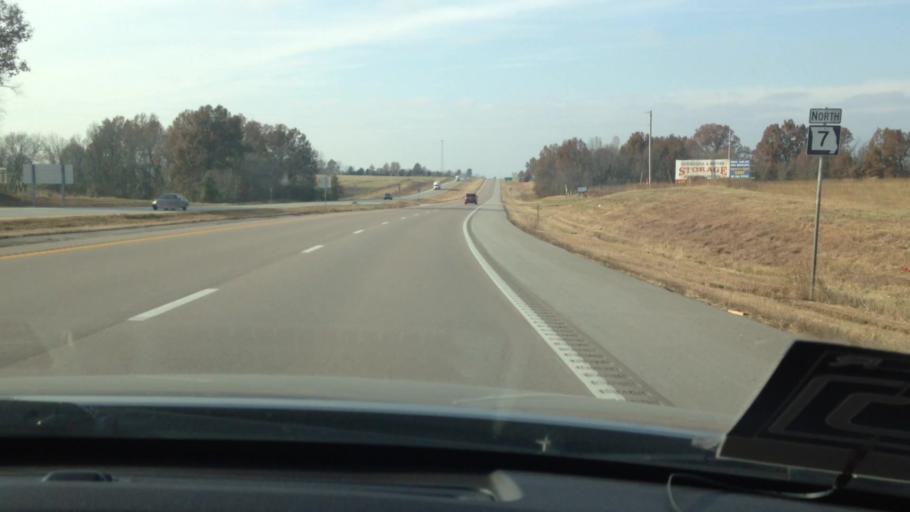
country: US
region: Missouri
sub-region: Cass County
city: Garden City
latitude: 38.4695
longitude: -94.0109
